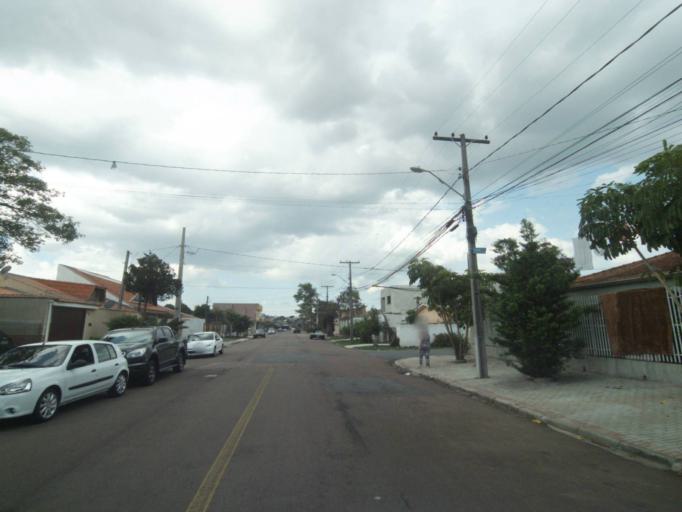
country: BR
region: Parana
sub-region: Sao Jose Dos Pinhais
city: Sao Jose dos Pinhais
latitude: -25.5298
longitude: -49.2696
